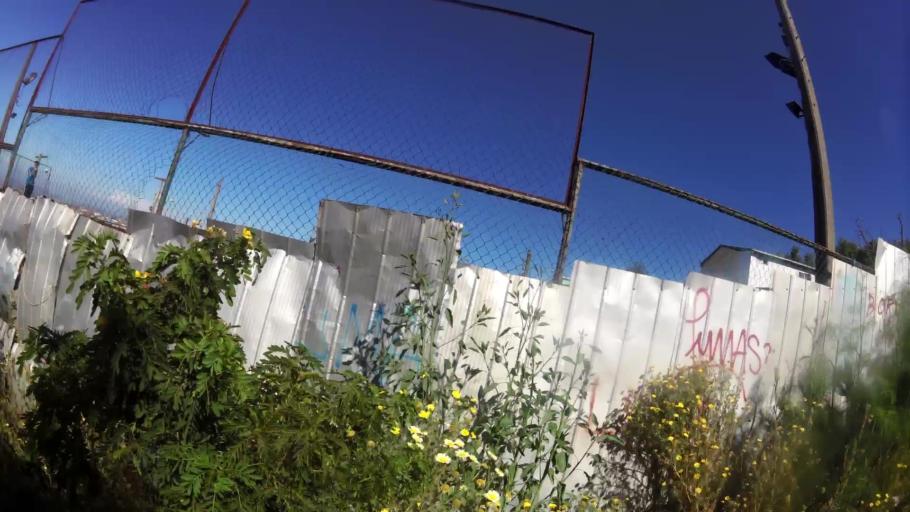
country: CL
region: Valparaiso
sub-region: Provincia de Valparaiso
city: Valparaiso
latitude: -33.0630
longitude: -71.6181
